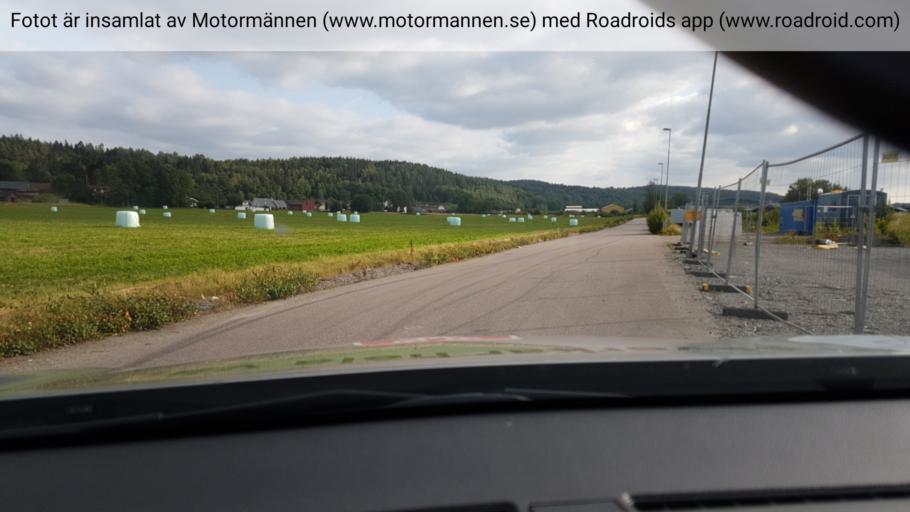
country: SE
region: Vaestra Goetaland
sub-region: Ale Kommun
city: Skepplanda
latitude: 57.9843
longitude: 12.2004
